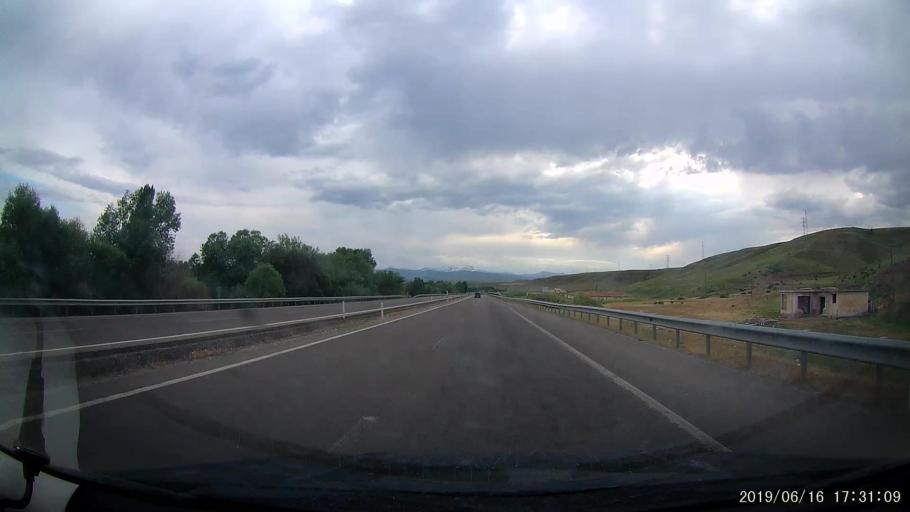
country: TR
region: Erzincan
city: Tercan
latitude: 39.7746
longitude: 40.3302
